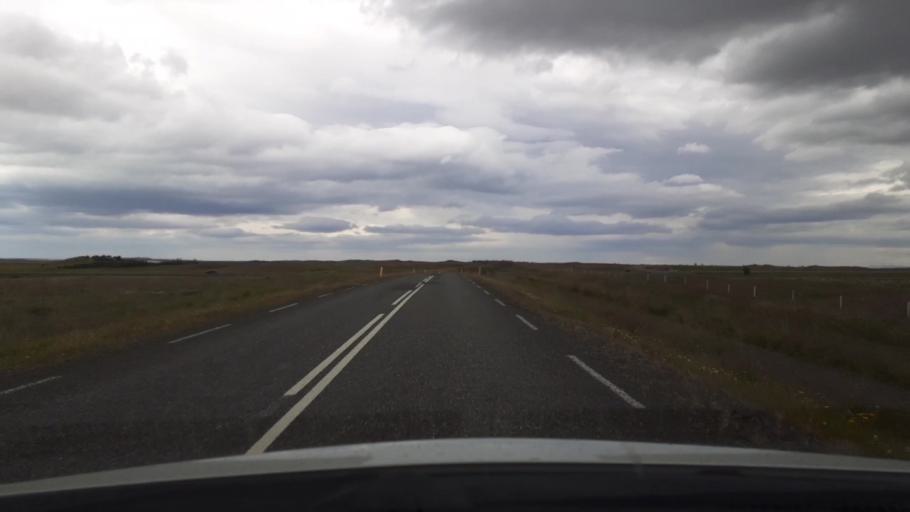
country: IS
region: West
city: Borgarnes
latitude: 64.5548
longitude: -21.7245
